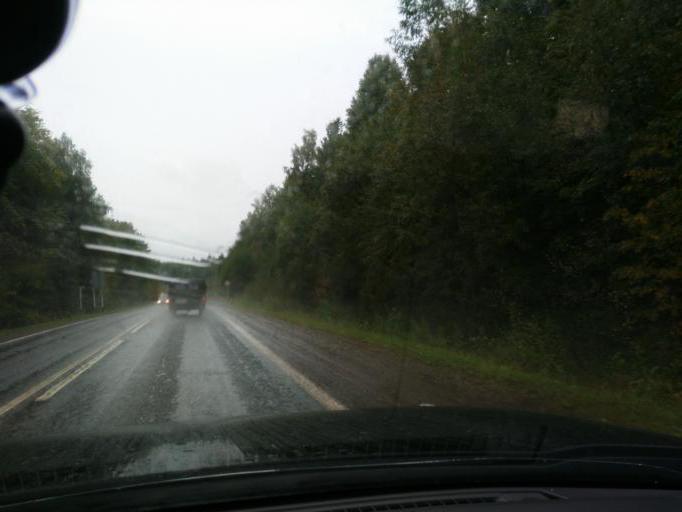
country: RU
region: Perm
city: Yugo-Kamskiy
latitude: 57.6270
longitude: 55.6172
